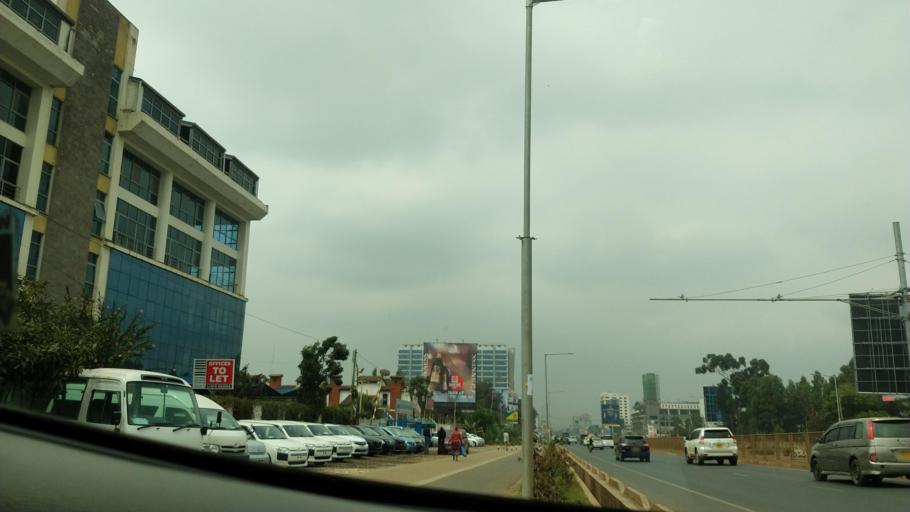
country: KE
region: Nairobi Area
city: Nairobi
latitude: -1.3000
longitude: 36.7769
